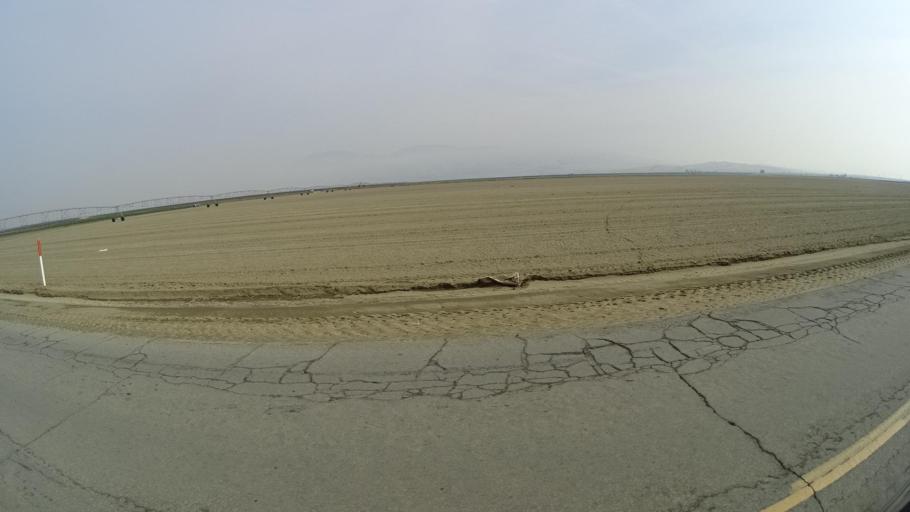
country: US
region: California
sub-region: Kern County
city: Arvin
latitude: 35.1573
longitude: -118.8782
